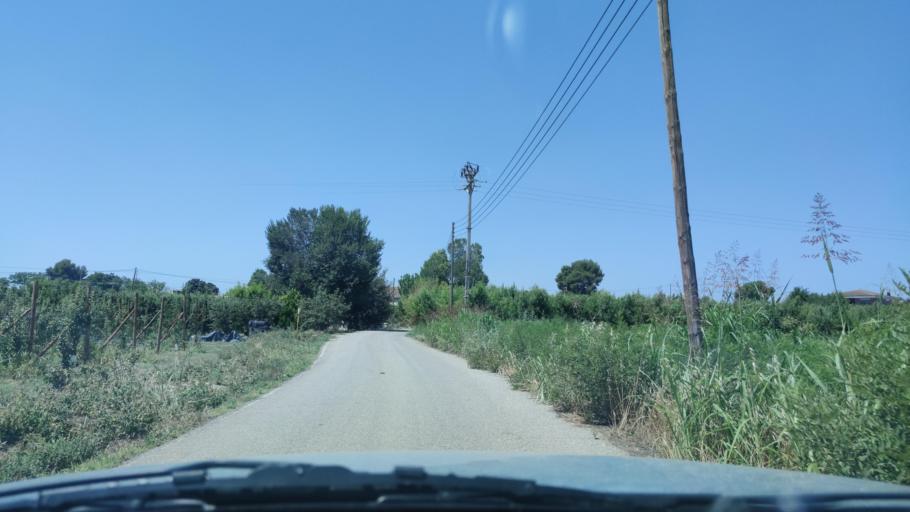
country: ES
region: Catalonia
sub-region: Provincia de Lleida
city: Torrefarrera
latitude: 41.6477
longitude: 0.5999
